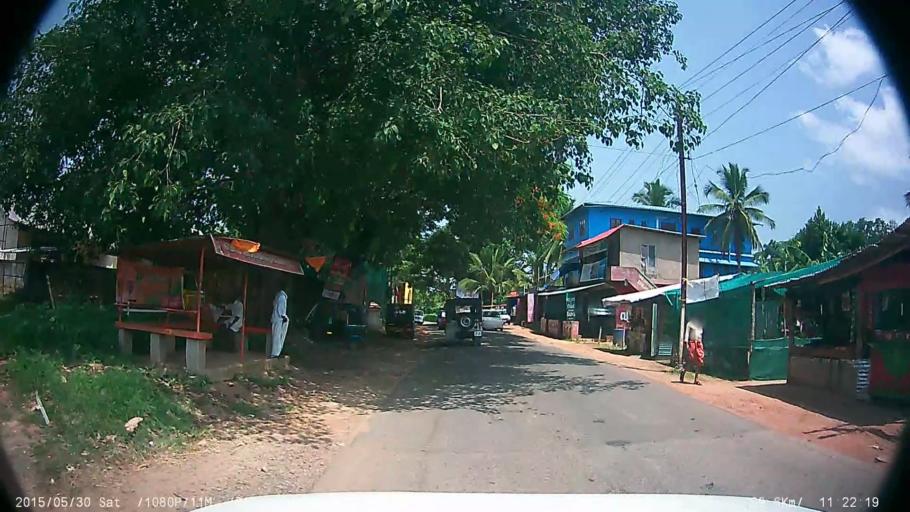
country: IN
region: Kerala
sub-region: Wayanad
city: Panamaram
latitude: 11.8023
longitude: 76.0316
